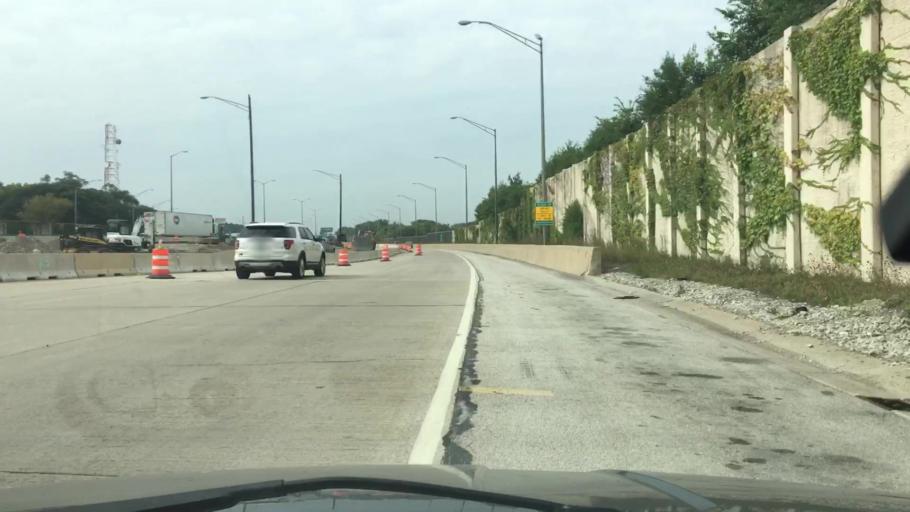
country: US
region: Illinois
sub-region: Cook County
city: Justice
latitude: 41.7403
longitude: -87.8273
